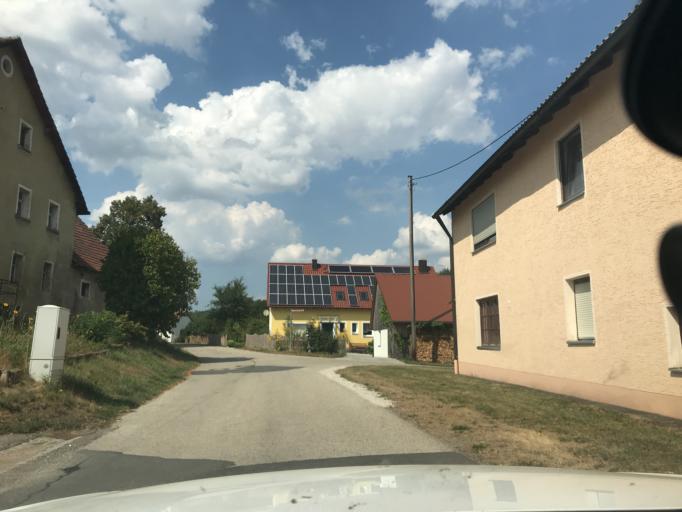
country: DE
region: Bavaria
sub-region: Upper Palatinate
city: Kirchenthumbach
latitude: 49.7568
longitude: 11.7165
